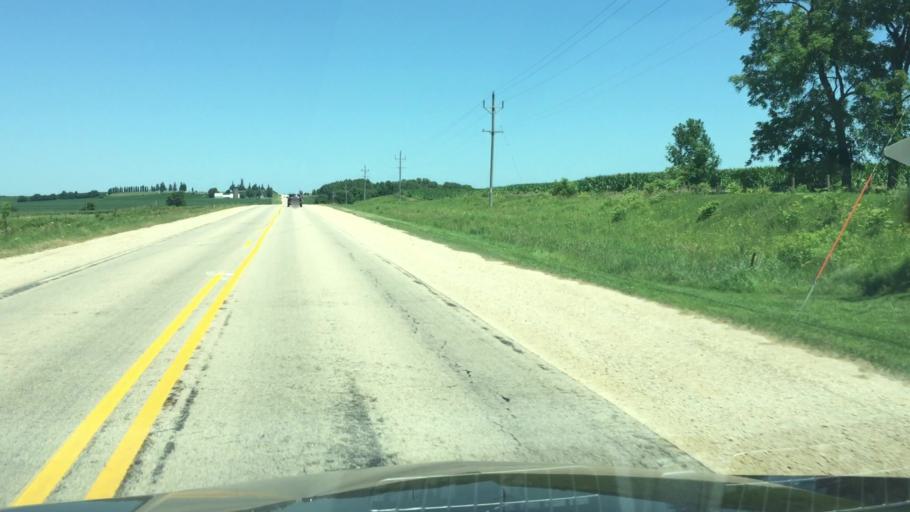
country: US
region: Iowa
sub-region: Cedar County
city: Mechanicsville
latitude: 41.9662
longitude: -91.1421
